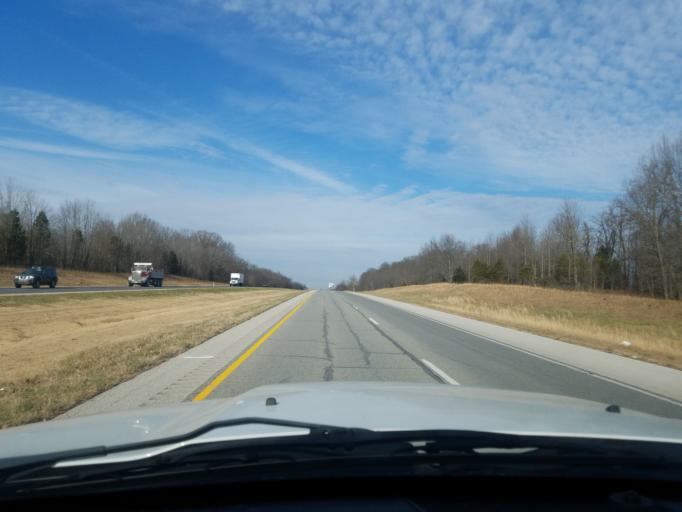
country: US
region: Indiana
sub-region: Monroe County
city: Bloomington
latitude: 39.0579
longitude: -86.5360
